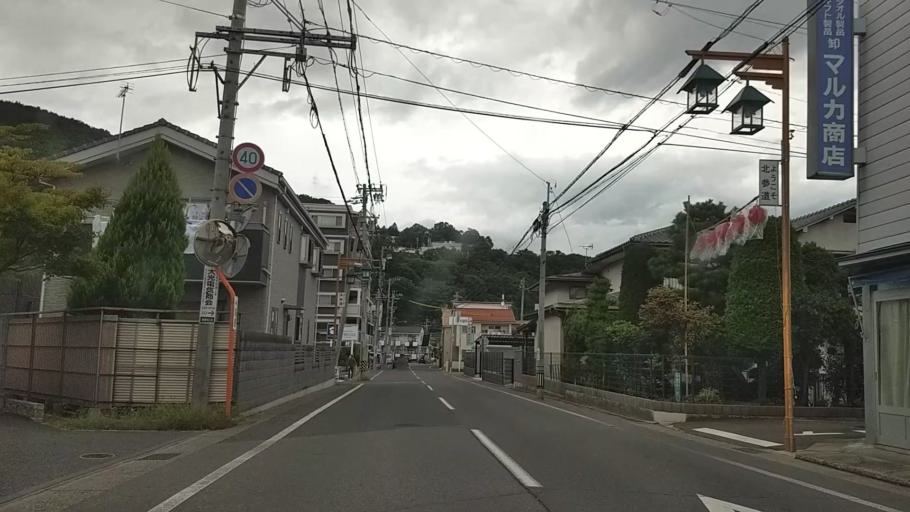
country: JP
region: Nagano
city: Nagano-shi
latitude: 36.6656
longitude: 138.1902
